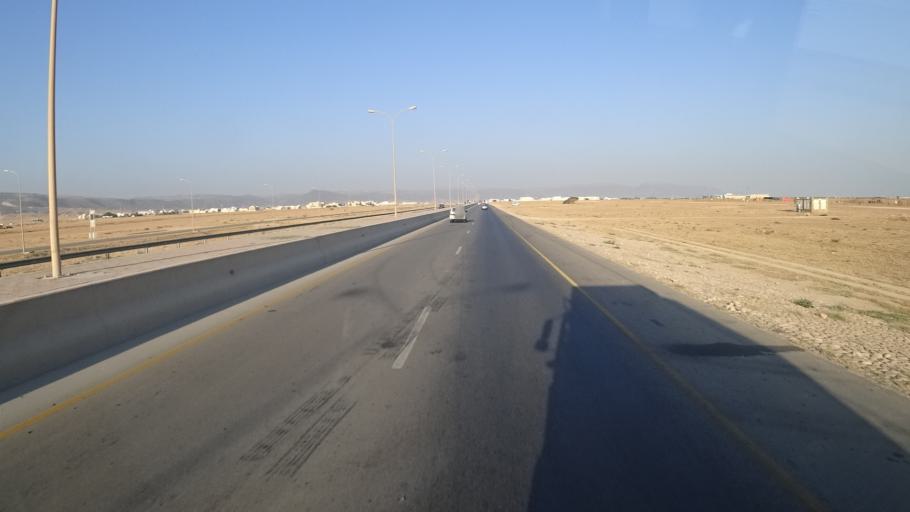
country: OM
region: Zufar
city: Salalah
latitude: 17.0810
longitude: 54.1220
